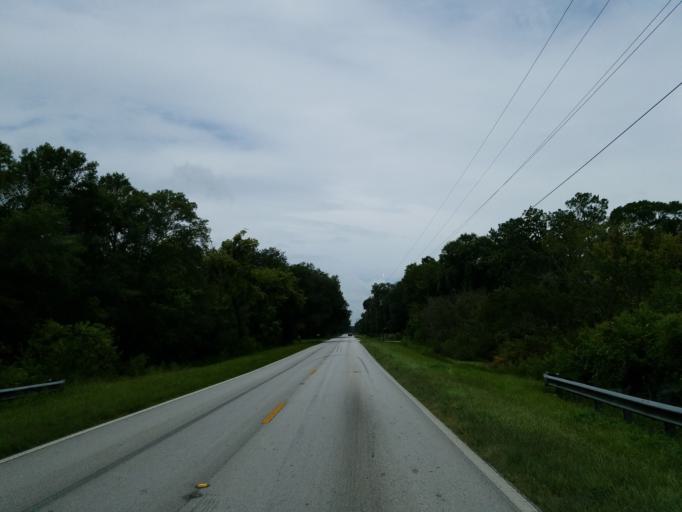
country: US
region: Florida
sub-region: Sumter County
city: Bushnell
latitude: 28.6689
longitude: -82.1689
